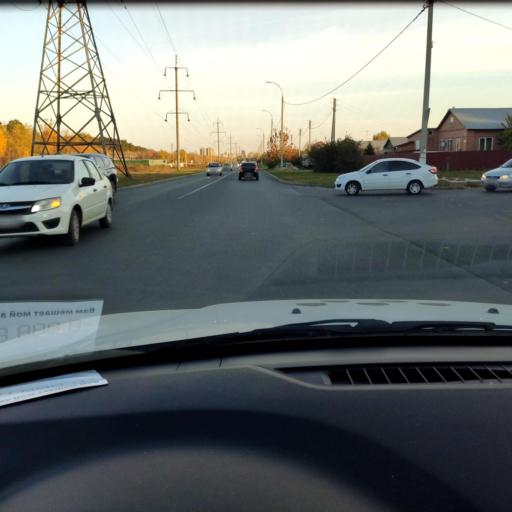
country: RU
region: Samara
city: Tol'yatti
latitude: 53.5140
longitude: 49.3954
